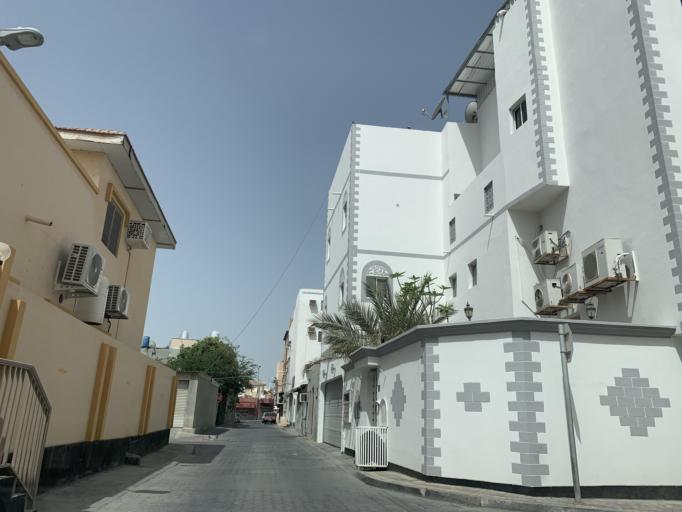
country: BH
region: Northern
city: Sitrah
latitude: 26.1337
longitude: 50.6010
